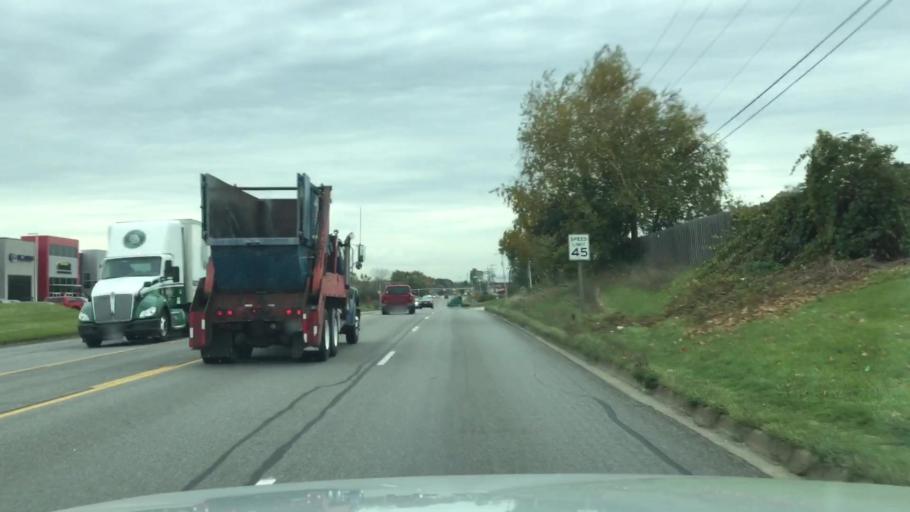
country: US
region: Michigan
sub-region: Kalamazoo County
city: Eastwood
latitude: 42.2535
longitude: -85.5309
